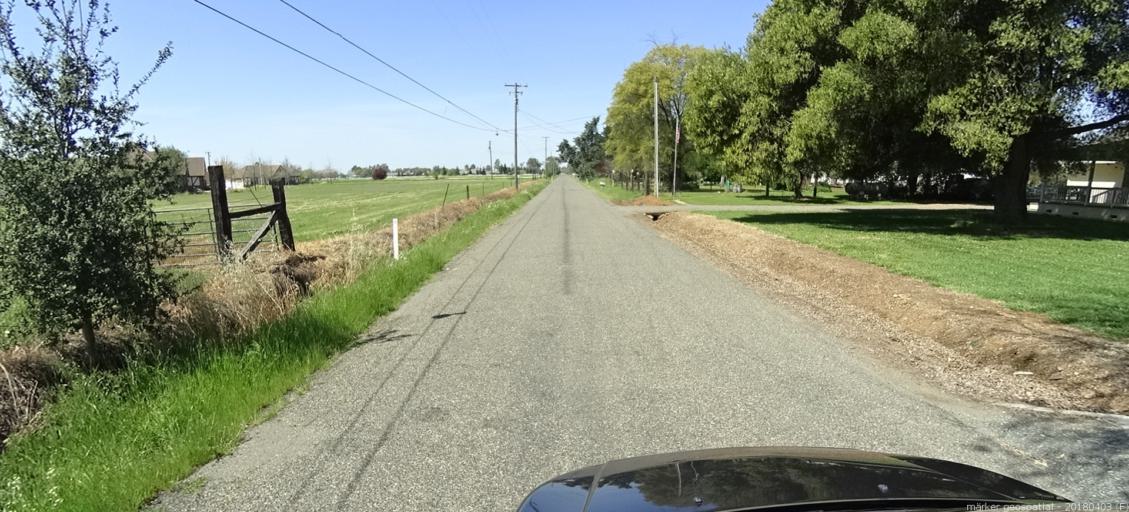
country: US
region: California
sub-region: Sacramento County
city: Wilton
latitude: 38.4018
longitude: -121.2623
